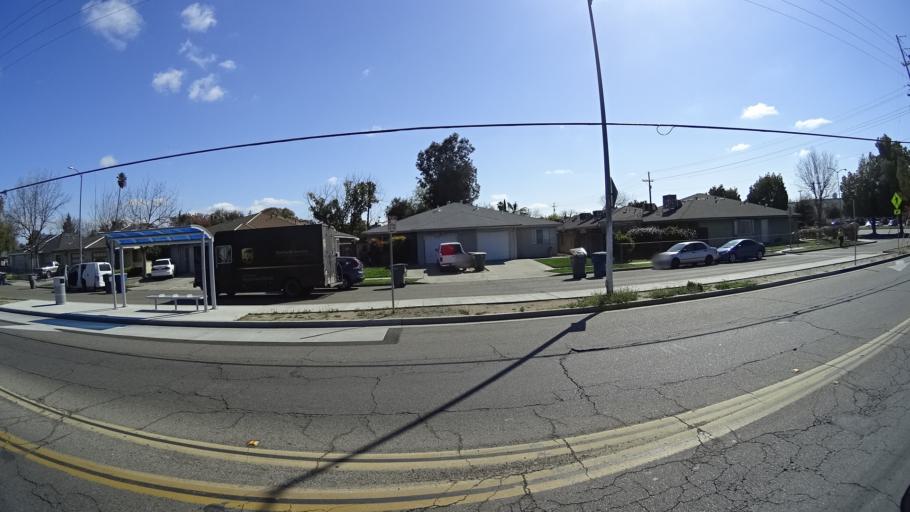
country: US
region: California
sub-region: Fresno County
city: West Park
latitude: 36.7944
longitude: -119.8805
